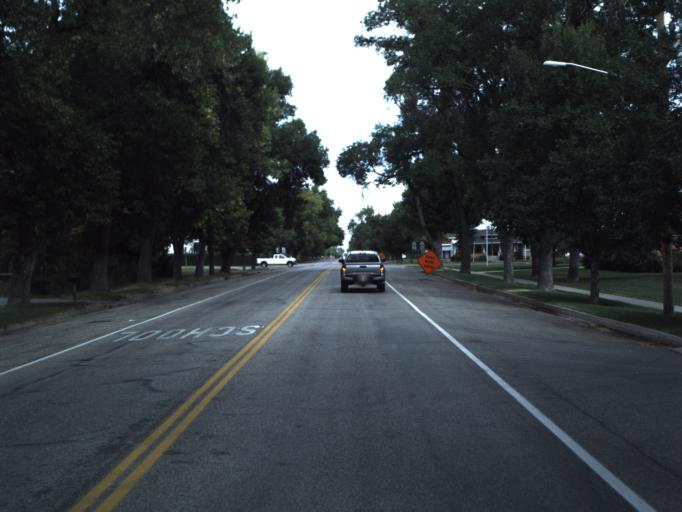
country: US
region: Utah
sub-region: Cache County
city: Wellsville
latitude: 41.6375
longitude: -111.9344
